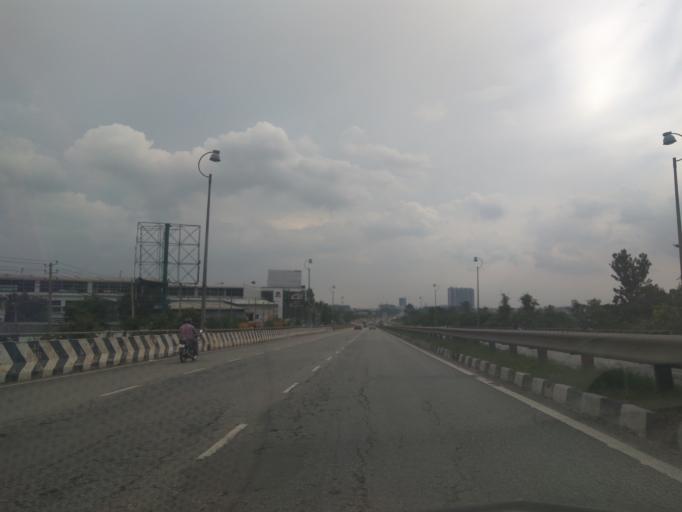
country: IN
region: Karnataka
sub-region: Bangalore Rural
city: Hoskote
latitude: 13.0348
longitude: 77.7346
